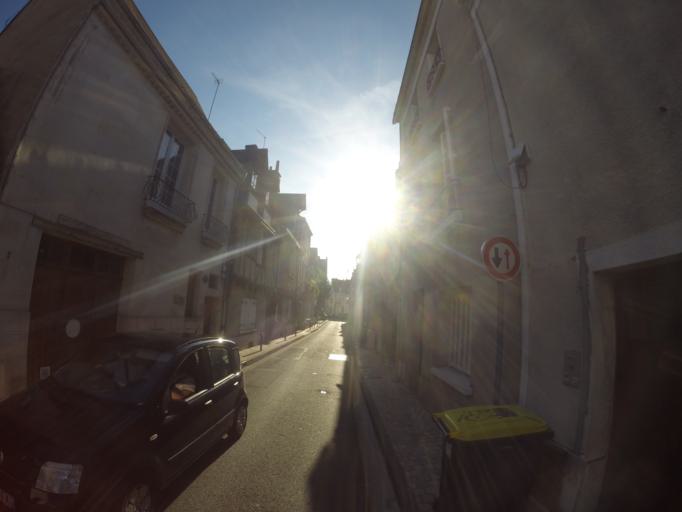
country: FR
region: Centre
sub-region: Departement d'Indre-et-Loire
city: Tours
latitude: 47.4030
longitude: 0.6954
